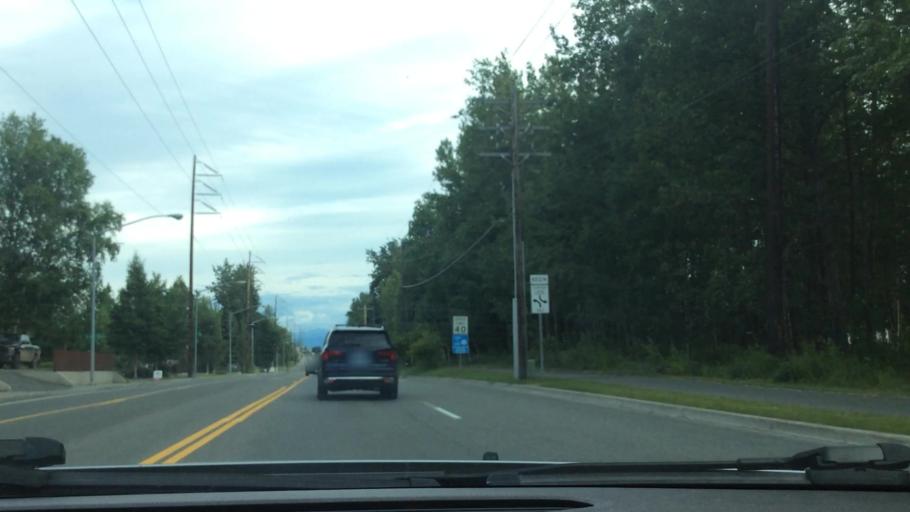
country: US
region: Alaska
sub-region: Anchorage Municipality
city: Anchorage
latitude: 61.1796
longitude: -149.8980
